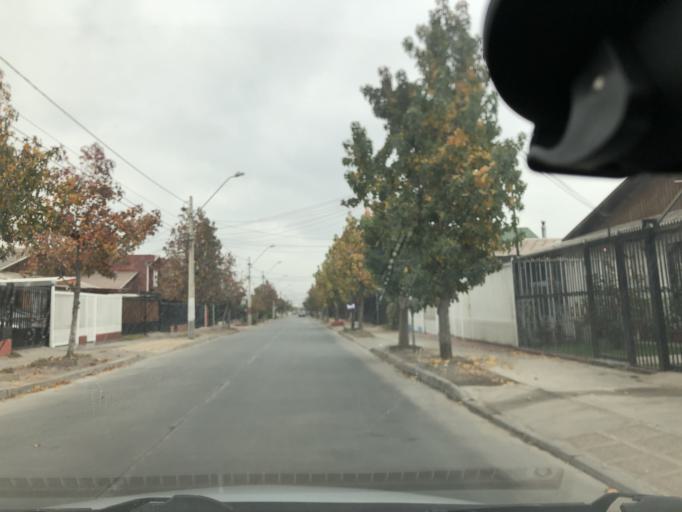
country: CL
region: Santiago Metropolitan
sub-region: Provincia de Santiago
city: La Pintana
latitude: -33.5772
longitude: -70.6066
